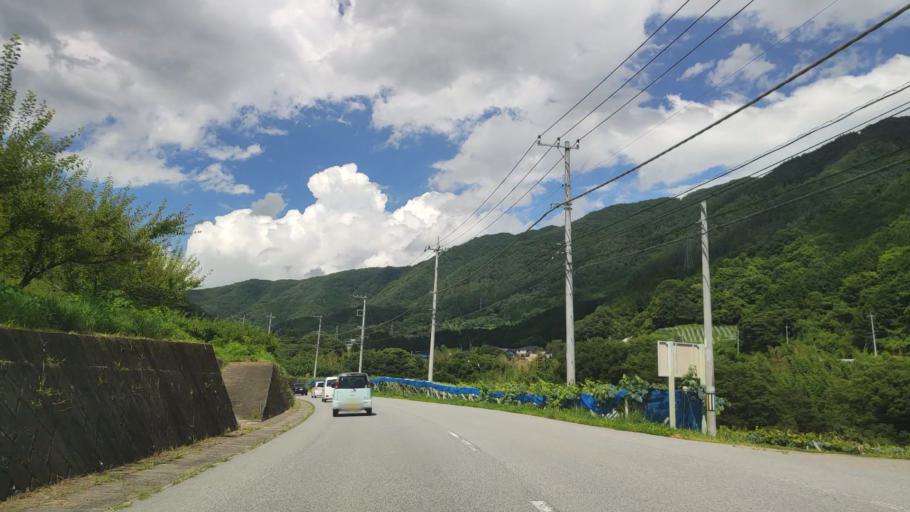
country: JP
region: Yamanashi
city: Enzan
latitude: 35.7600
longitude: 138.7318
